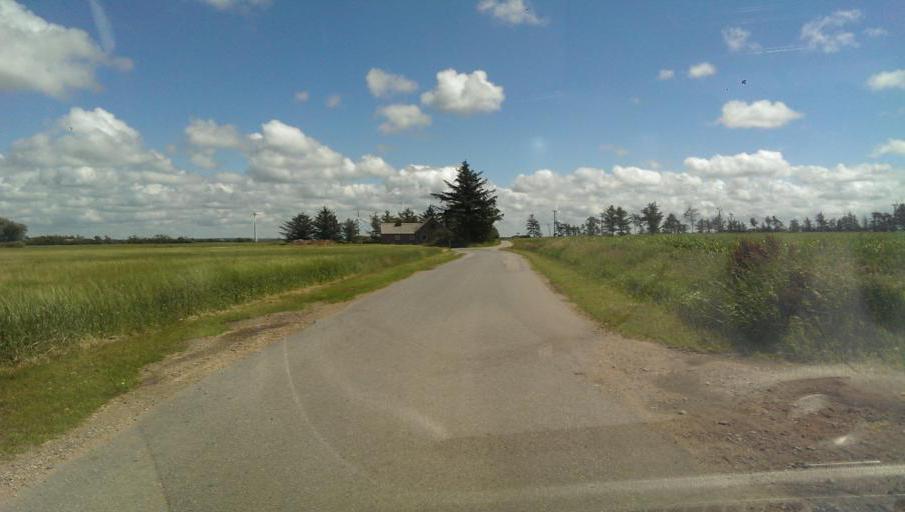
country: DK
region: Central Jutland
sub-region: Holstebro Kommune
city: Ulfborg
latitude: 56.2347
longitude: 8.2209
